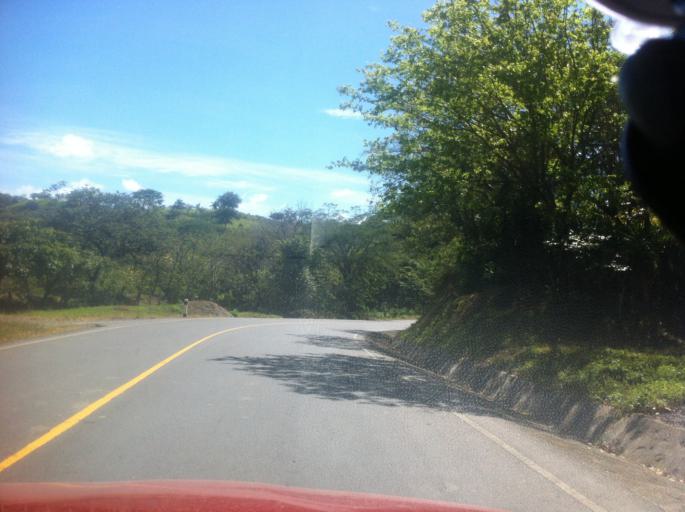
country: NI
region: Matagalpa
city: San Ramon
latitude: 12.8864
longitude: -85.8397
